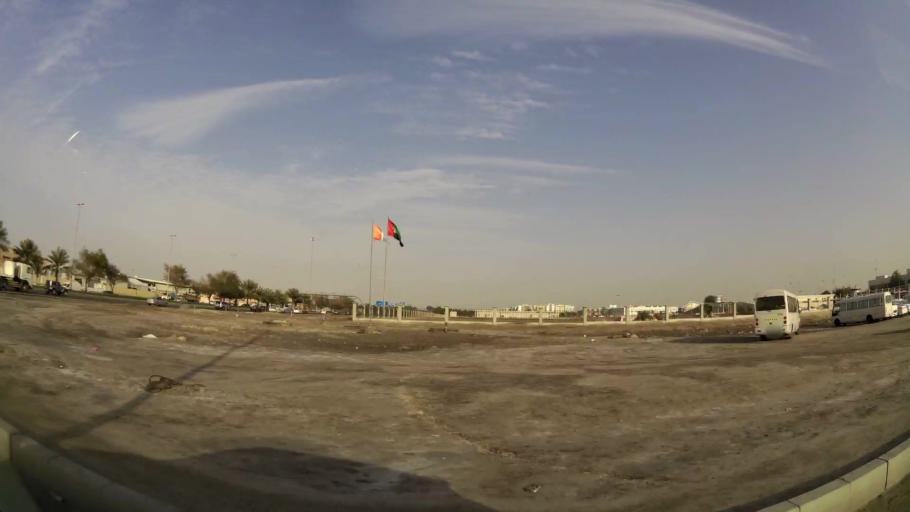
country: AE
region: Abu Dhabi
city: Abu Dhabi
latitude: 24.3461
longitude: 54.5173
